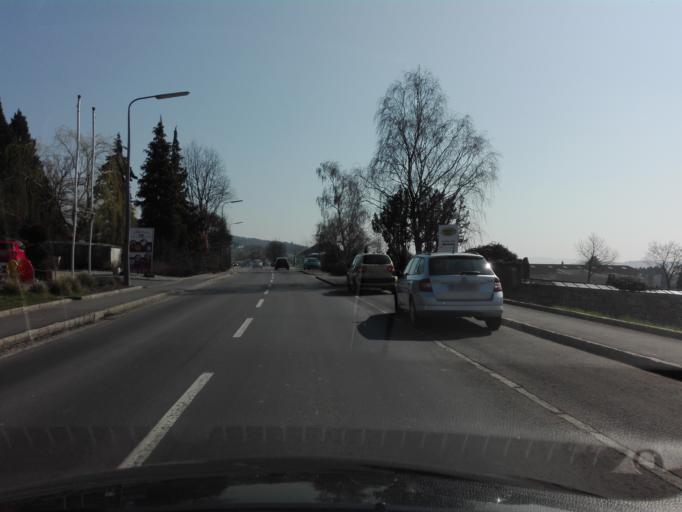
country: AT
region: Upper Austria
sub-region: Politischer Bezirk Urfahr-Umgebung
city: Gallneukirchen
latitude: 48.3549
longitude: 14.4225
